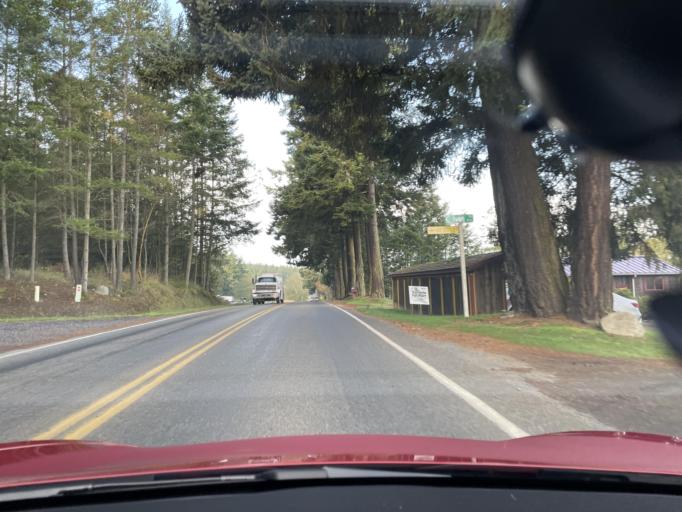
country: US
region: Washington
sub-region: San Juan County
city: Friday Harbor
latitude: 48.5399
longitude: -123.0384
